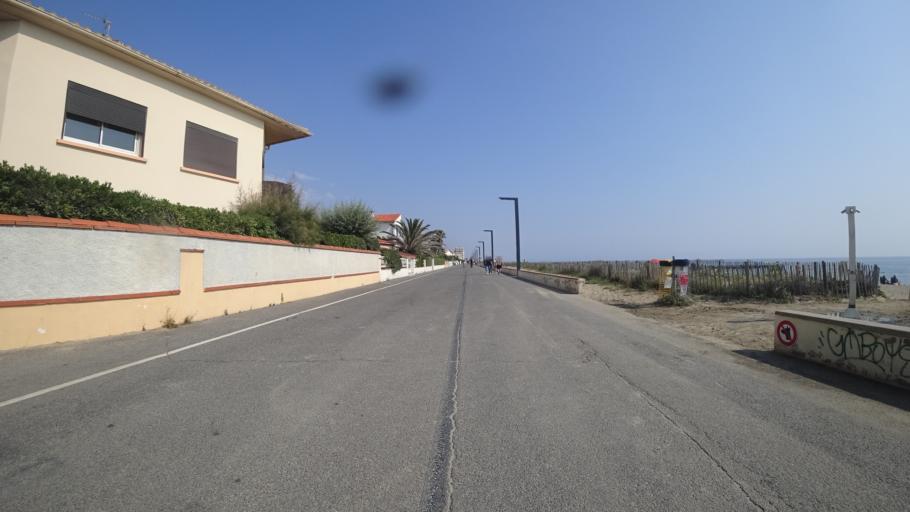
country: FR
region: Languedoc-Roussillon
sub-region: Departement des Pyrenees-Orientales
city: Saint-Cyprien-Plage
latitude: 42.6250
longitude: 3.0363
